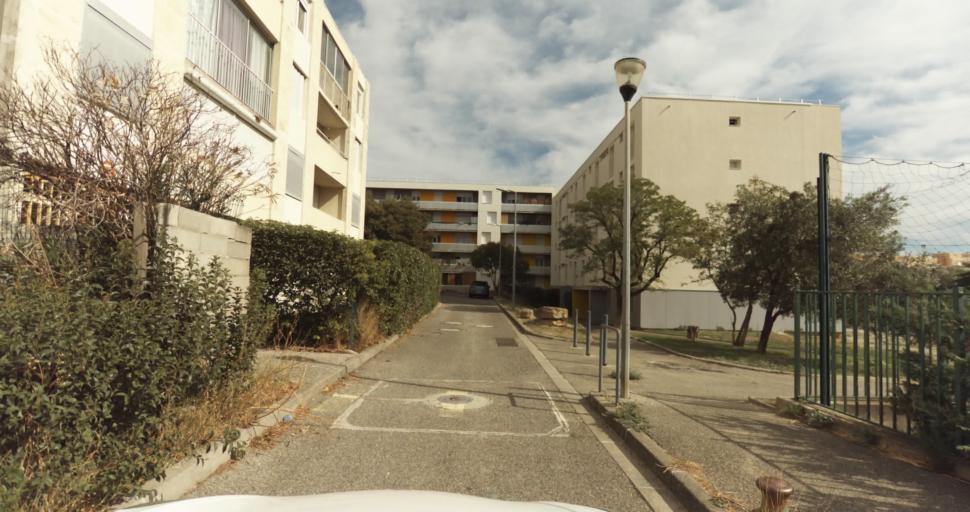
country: FR
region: Provence-Alpes-Cote d'Azur
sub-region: Departement des Bouches-du-Rhone
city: Miramas
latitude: 43.5943
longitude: 5.0076
